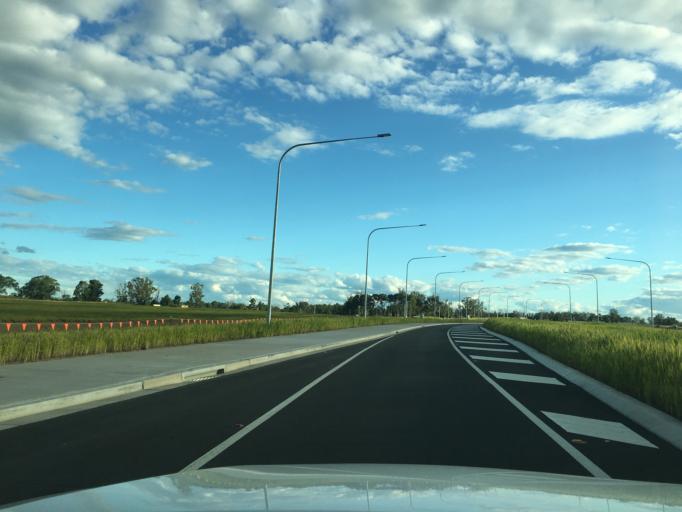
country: AU
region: New South Wales
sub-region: Liverpool
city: Bringelly
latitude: -33.8803
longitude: 150.7457
